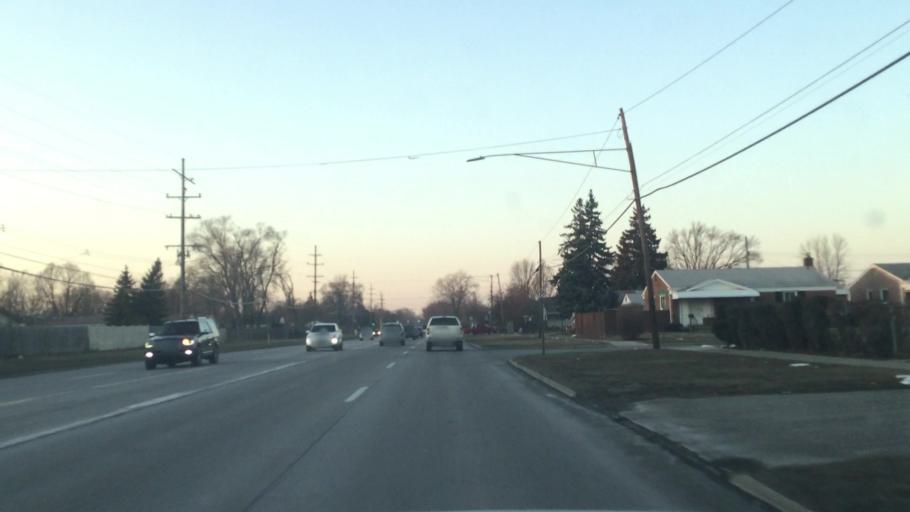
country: US
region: Michigan
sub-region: Wayne County
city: Livonia
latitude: 42.3498
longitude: -83.3514
